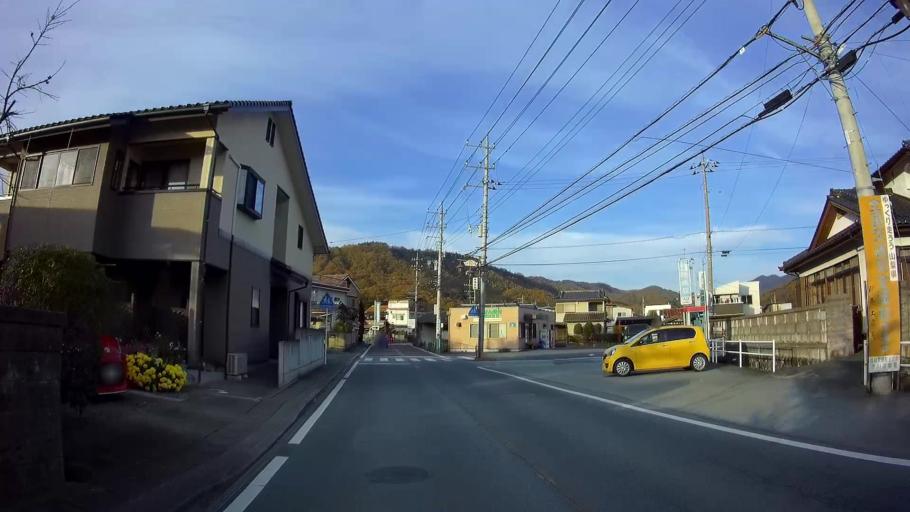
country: JP
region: Yamanashi
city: Ryuo
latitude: 35.4906
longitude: 138.4598
